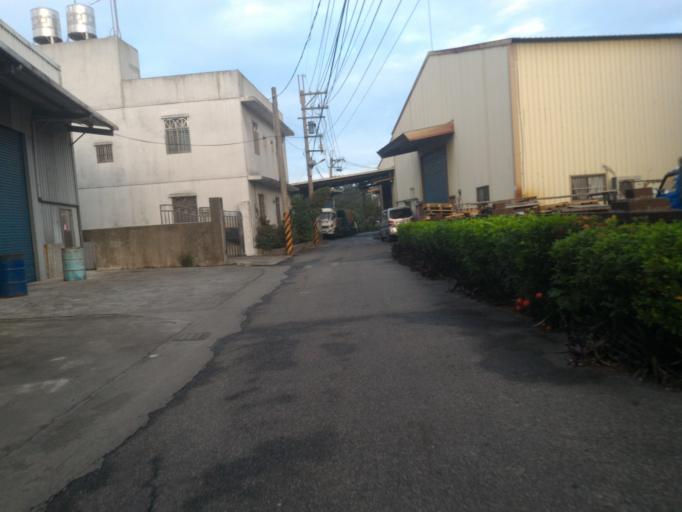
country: TW
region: Taiwan
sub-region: Taoyuan
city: Taoyuan
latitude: 24.9489
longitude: 121.3968
